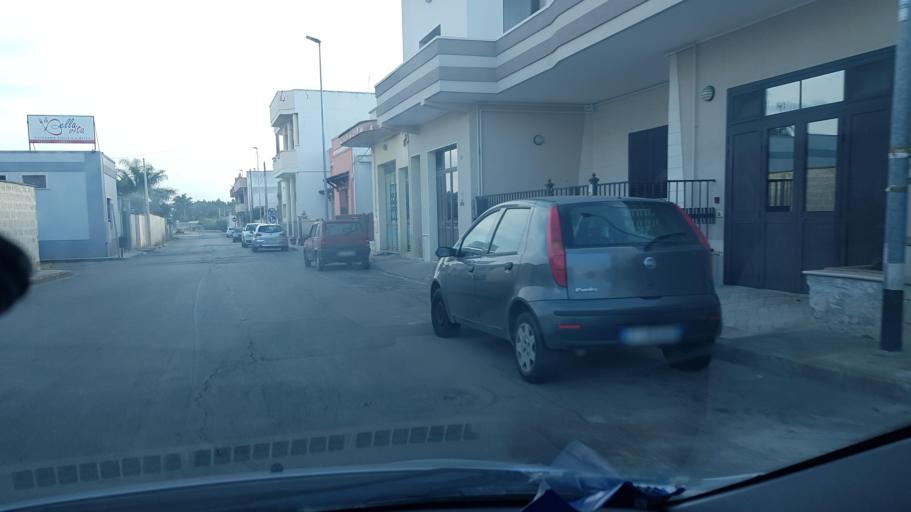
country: IT
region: Apulia
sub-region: Provincia di Lecce
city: Carmiano
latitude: 40.3449
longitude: 18.0376
